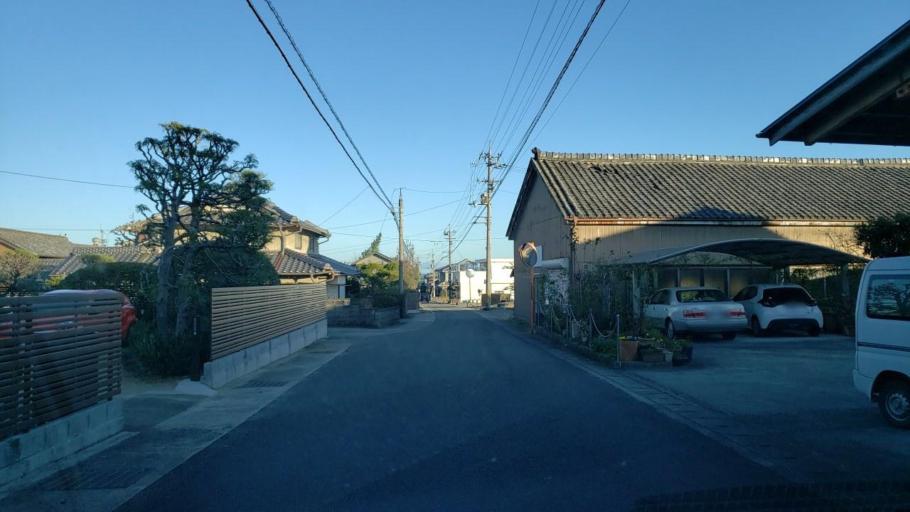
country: JP
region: Tokushima
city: Wakimachi
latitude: 34.0917
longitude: 134.2446
